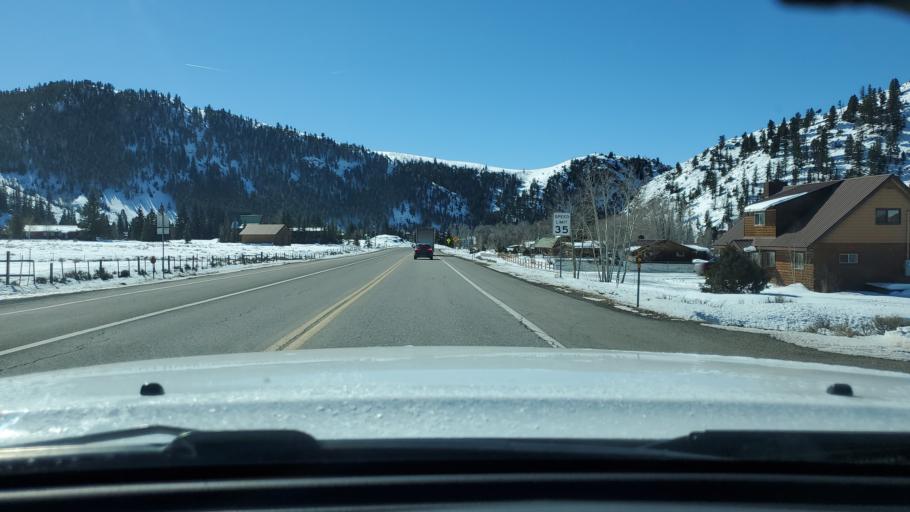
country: US
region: Colorado
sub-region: Gunnison County
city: Gunnison
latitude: 38.6681
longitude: -106.8457
